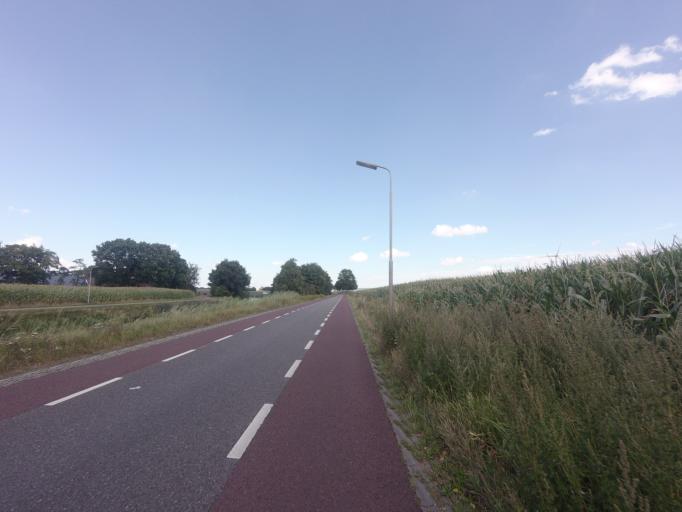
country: NL
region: Overijssel
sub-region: Gemeente Twenterand
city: Den Ham
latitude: 52.5725
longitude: 6.4471
